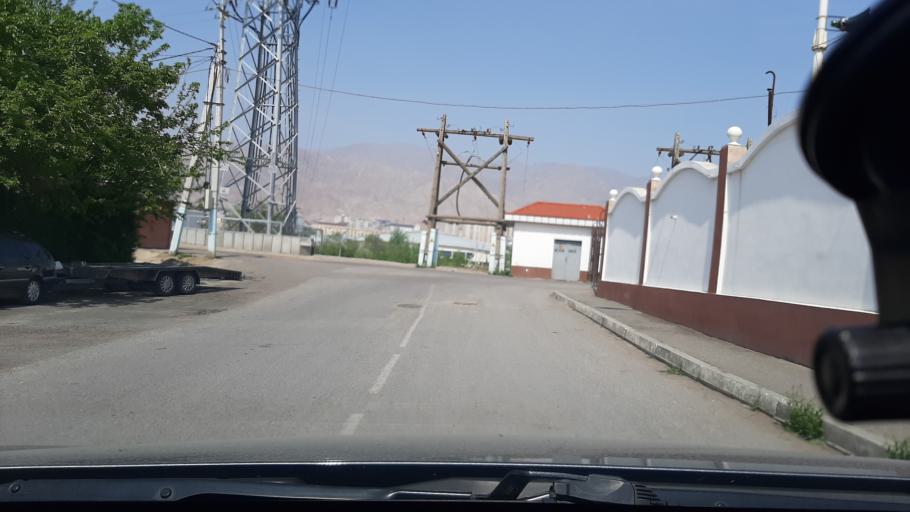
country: TJ
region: Viloyati Sughd
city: Khujand
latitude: 40.2881
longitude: 69.6125
